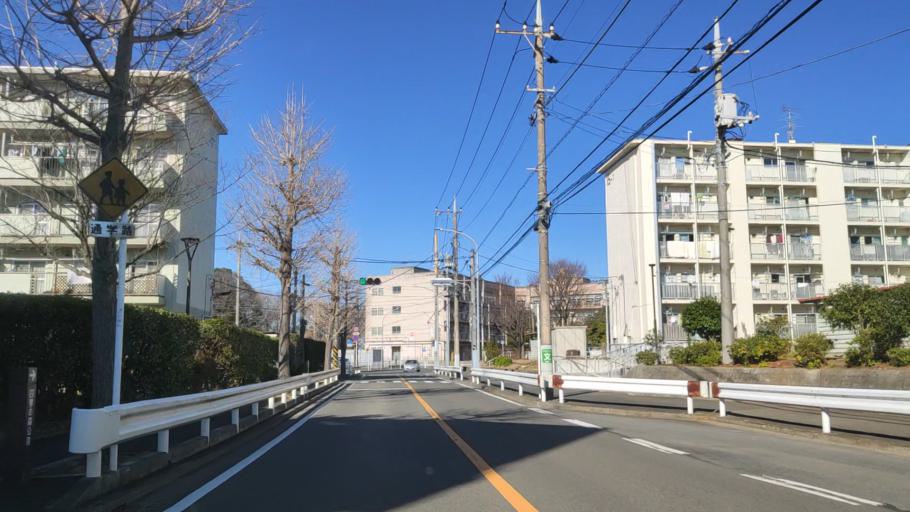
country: JP
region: Kanagawa
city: Minami-rinkan
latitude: 35.5021
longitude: 139.5302
